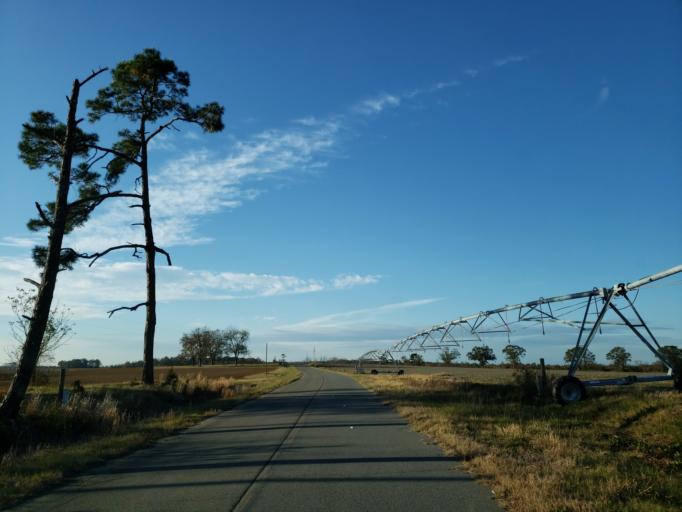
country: US
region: Georgia
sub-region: Dooly County
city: Unadilla
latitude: 32.2034
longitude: -83.7691
